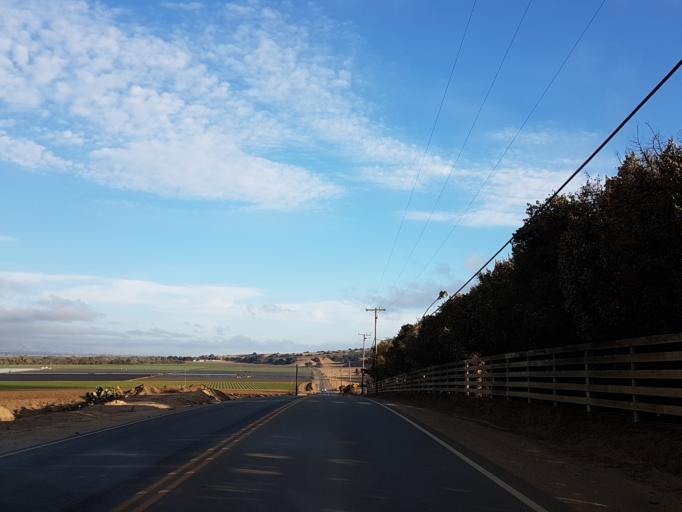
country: US
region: California
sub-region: Monterey County
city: Chualar
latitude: 36.5875
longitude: -121.6027
